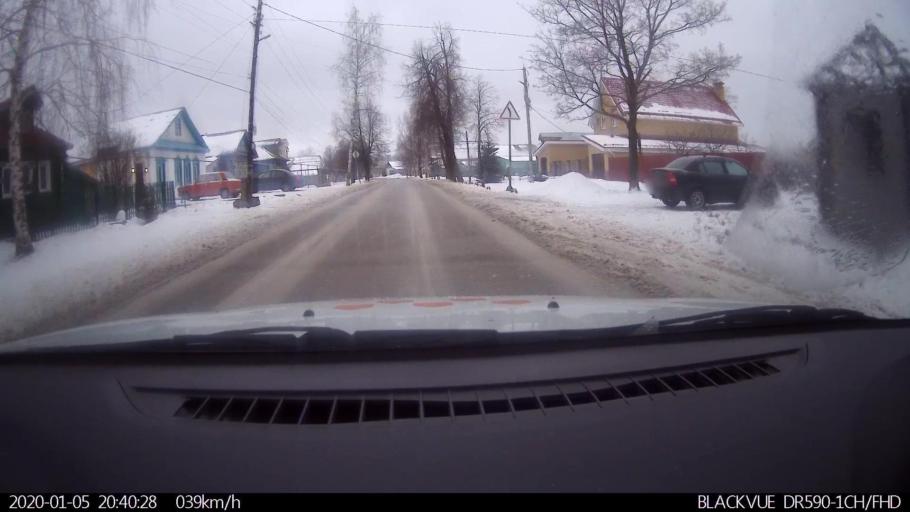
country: RU
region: Nizjnij Novgorod
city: Lukino
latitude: 56.4096
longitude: 43.7288
